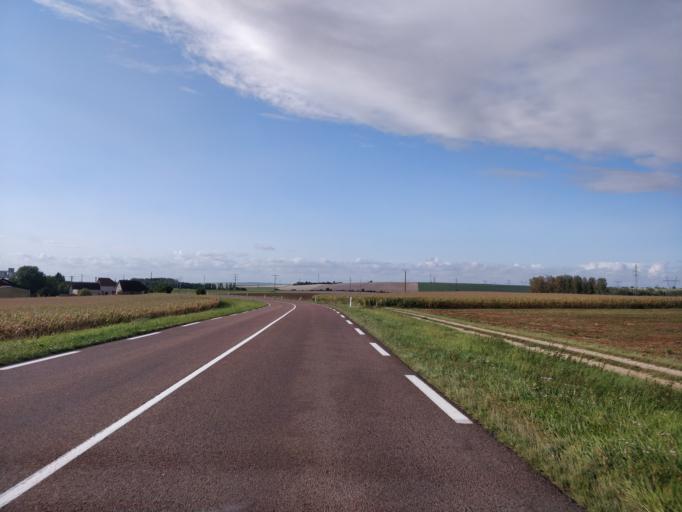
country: FR
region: Champagne-Ardenne
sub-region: Departement de l'Aube
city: Verrieres
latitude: 48.2777
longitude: 4.1978
